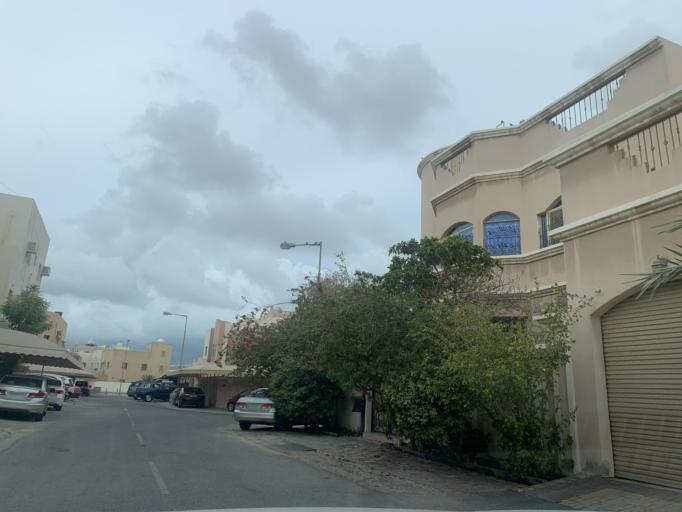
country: BH
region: Muharraq
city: Al Hadd
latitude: 26.2790
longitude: 50.6440
